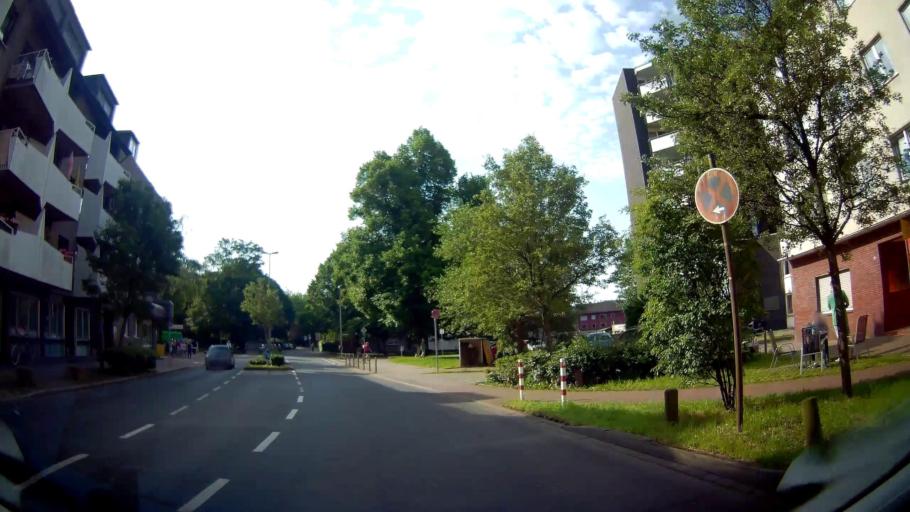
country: DE
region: North Rhine-Westphalia
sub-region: Regierungsbezirk Arnsberg
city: Herne
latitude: 51.5287
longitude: 7.2286
